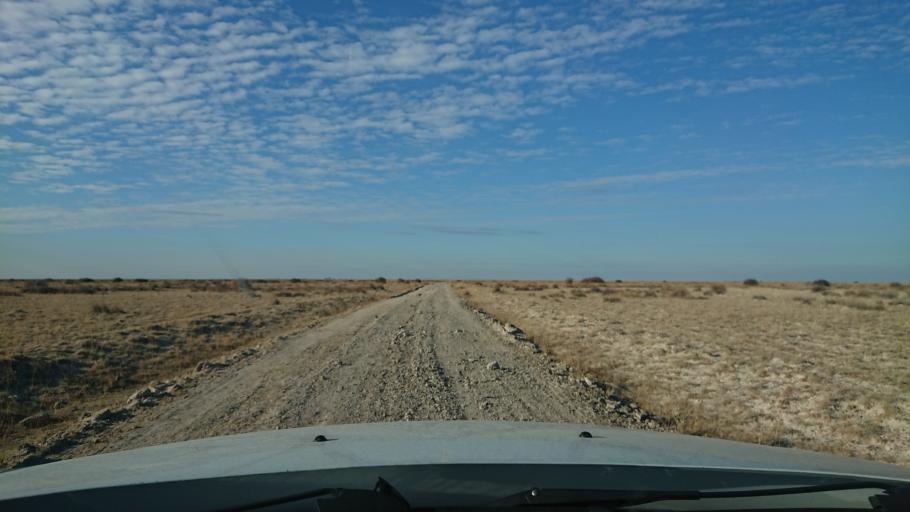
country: TR
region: Aksaray
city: Eskil
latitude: 38.5472
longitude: 33.3186
